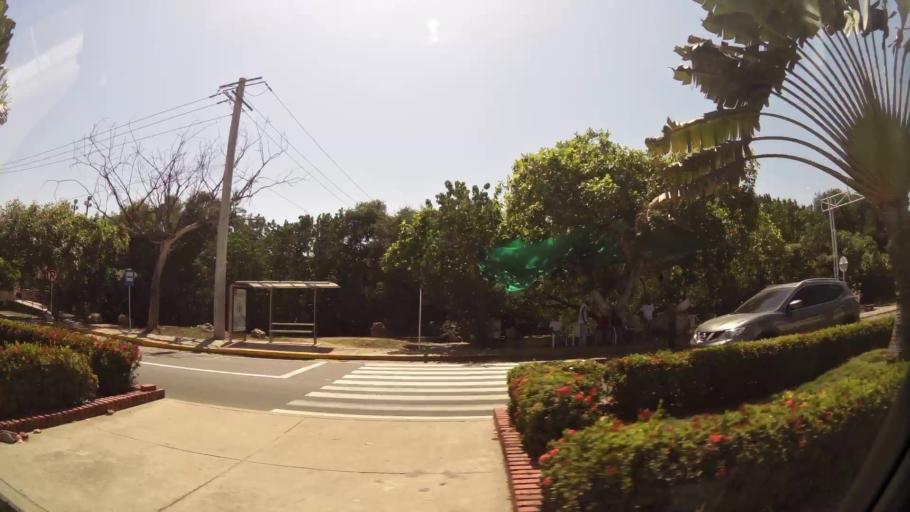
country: CO
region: Bolivar
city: Cartagena
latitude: 10.4430
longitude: -75.5189
